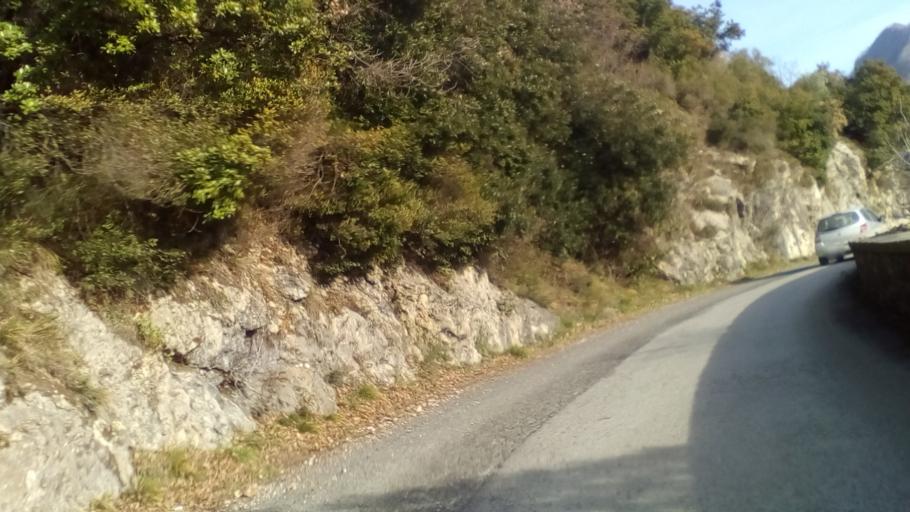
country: IT
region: Tuscany
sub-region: Provincia di Massa-Carrara
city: Massa
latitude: 44.0834
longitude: 10.1211
